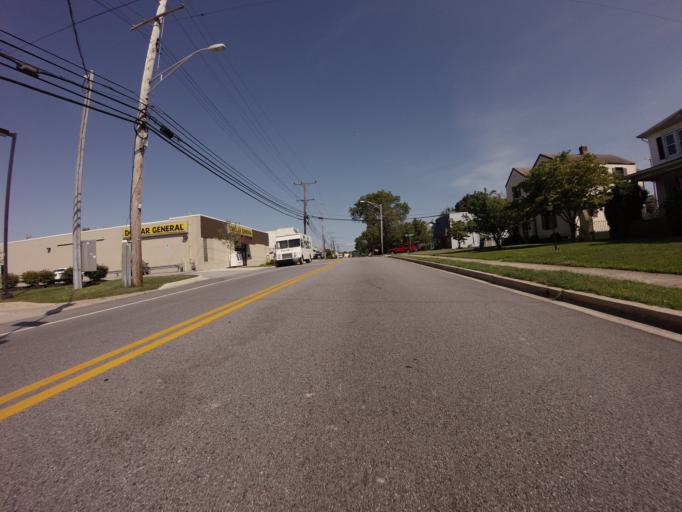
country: US
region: Maryland
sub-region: Baltimore County
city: Edgemere
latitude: 39.2424
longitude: -76.4495
